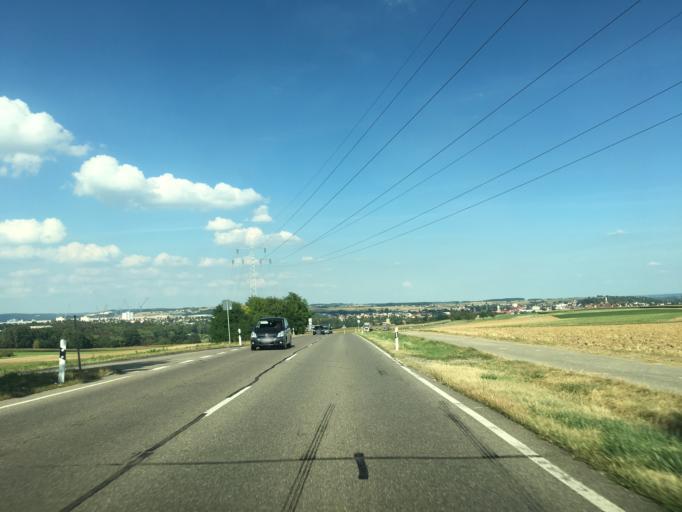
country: DE
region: Baden-Wuerttemberg
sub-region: Tuebingen Region
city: Dettingen
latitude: 48.2744
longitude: 9.6867
